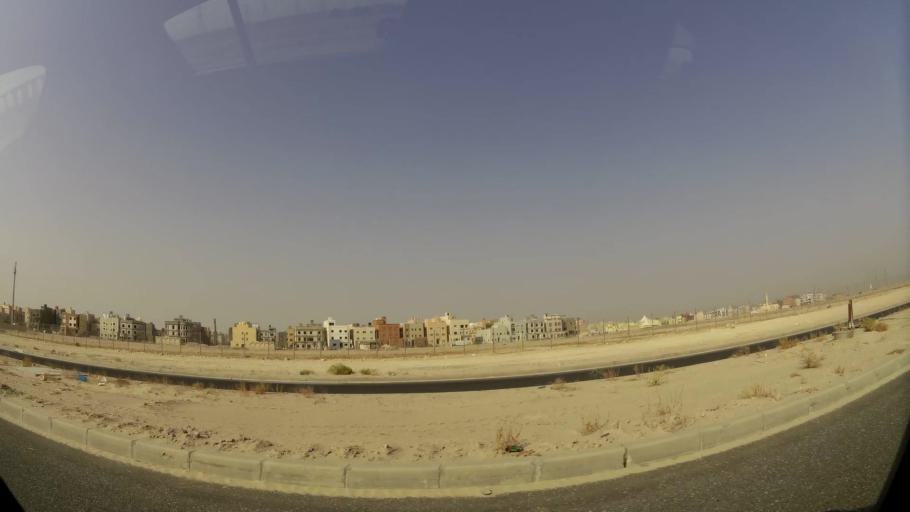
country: KW
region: Muhafazat al Jahra'
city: Al Jahra'
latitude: 29.3513
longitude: 47.7813
